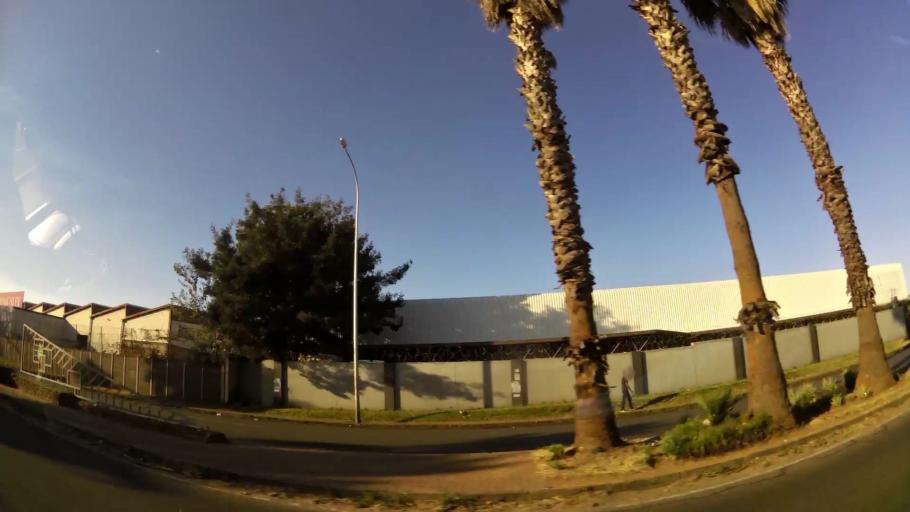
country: ZA
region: Gauteng
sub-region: City of Johannesburg Metropolitan Municipality
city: Roodepoort
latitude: -26.1557
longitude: 27.8670
